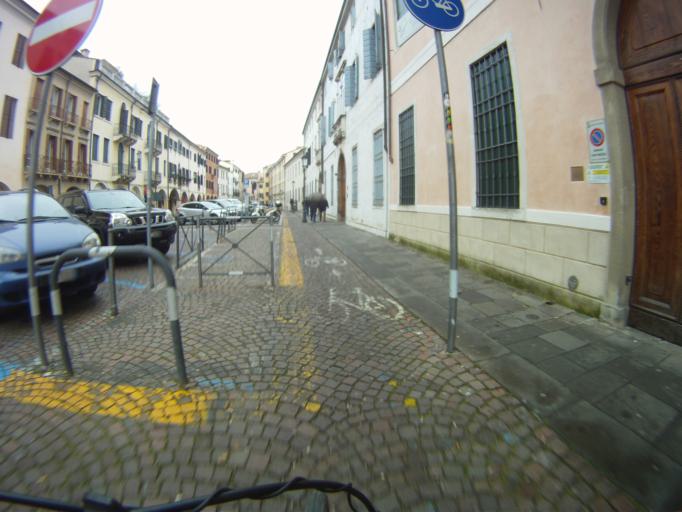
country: IT
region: Veneto
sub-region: Provincia di Padova
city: Padova
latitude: 45.4017
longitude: 11.8814
